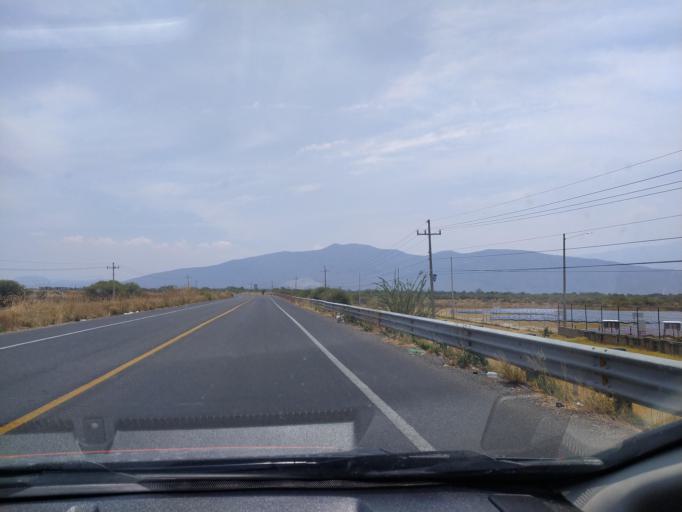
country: MX
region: Jalisco
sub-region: Zacoalco de Torres
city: Barranca de Otates (Barranca de Otatan)
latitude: 20.3129
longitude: -103.5920
